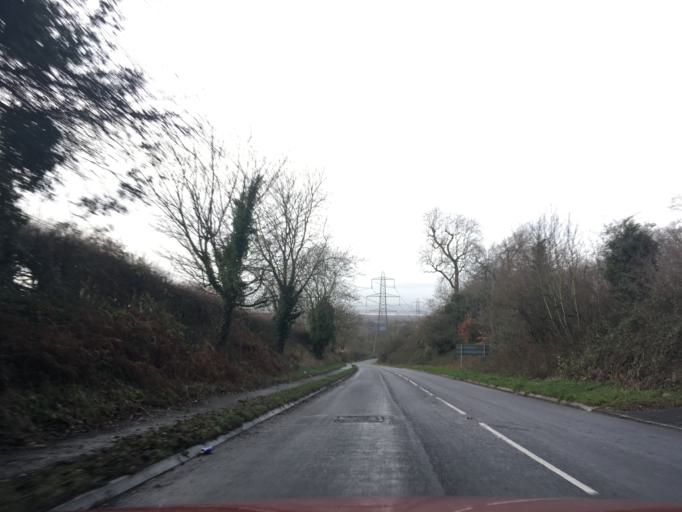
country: GB
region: England
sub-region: South Gloucestershire
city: Almondsbury
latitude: 51.5634
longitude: -2.5574
